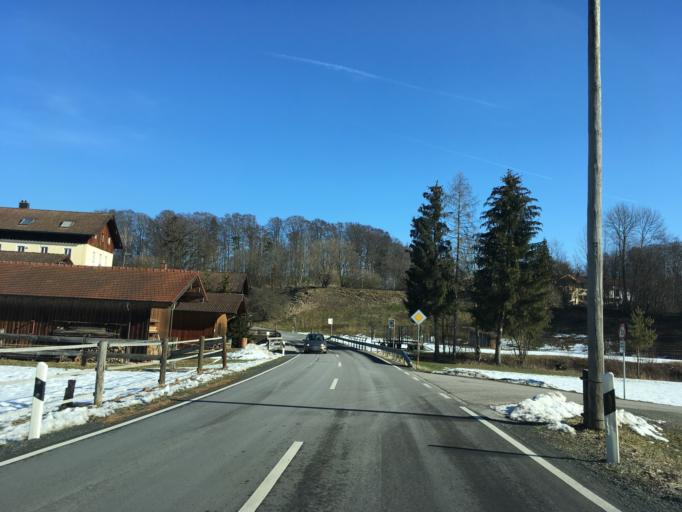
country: DE
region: Bavaria
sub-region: Upper Bavaria
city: Ramerberg
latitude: 48.0294
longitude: 12.1437
